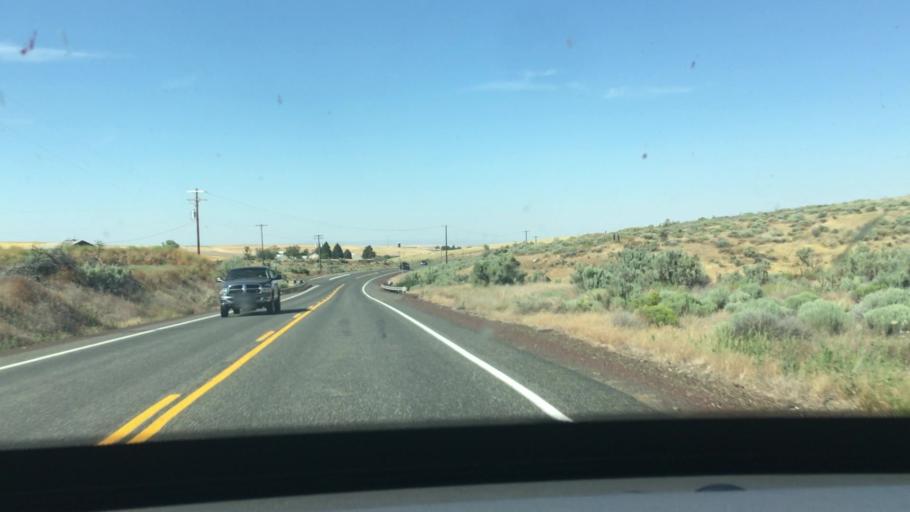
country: US
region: Oregon
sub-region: Sherman County
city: Moro
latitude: 45.4520
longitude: -120.7519
